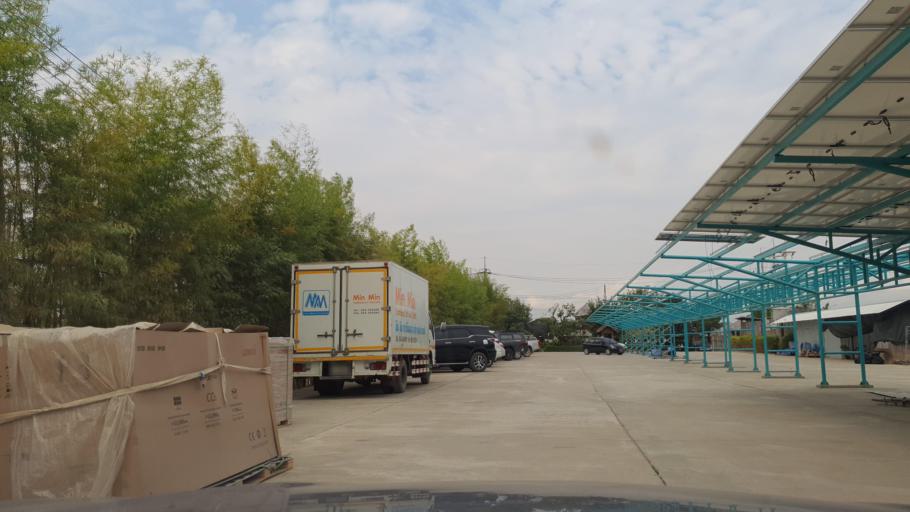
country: TH
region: Chiang Mai
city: Hang Dong
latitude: 18.6803
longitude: 98.9609
